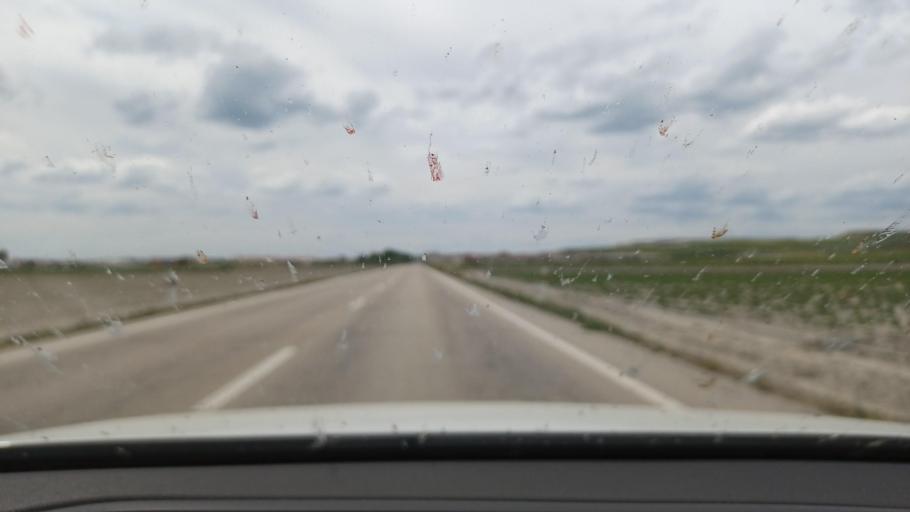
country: ES
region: Castille and Leon
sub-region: Provincia de Segovia
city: Frumales
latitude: 41.3833
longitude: -4.2317
